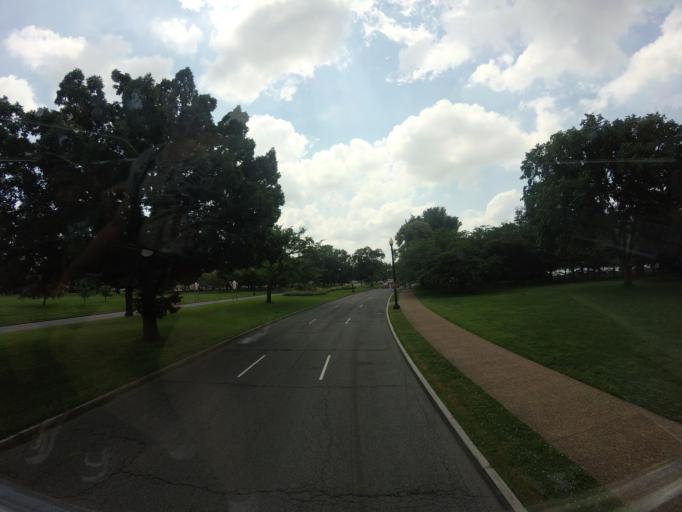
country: US
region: Washington, D.C.
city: Washington, D.C.
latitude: 38.8862
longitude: -77.0353
